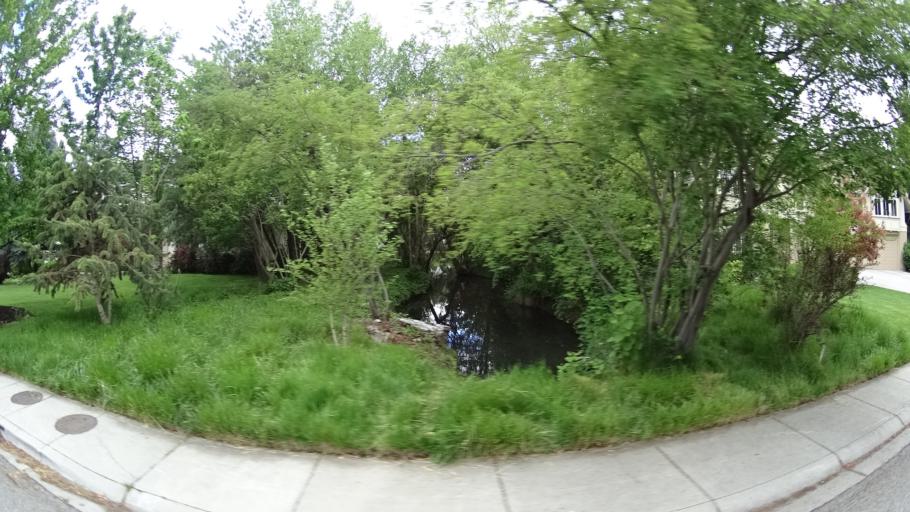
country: US
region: Idaho
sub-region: Ada County
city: Eagle
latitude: 43.6702
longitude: -116.2937
